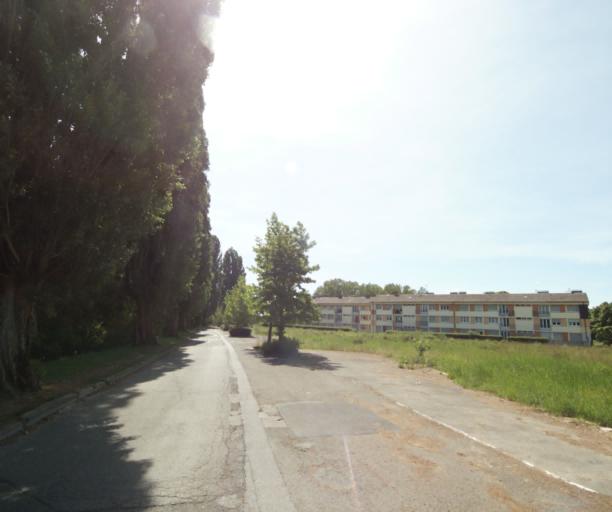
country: FR
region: Champagne-Ardenne
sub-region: Departement des Ardennes
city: Prix-les-Mezieres
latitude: 49.7608
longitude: 4.6936
